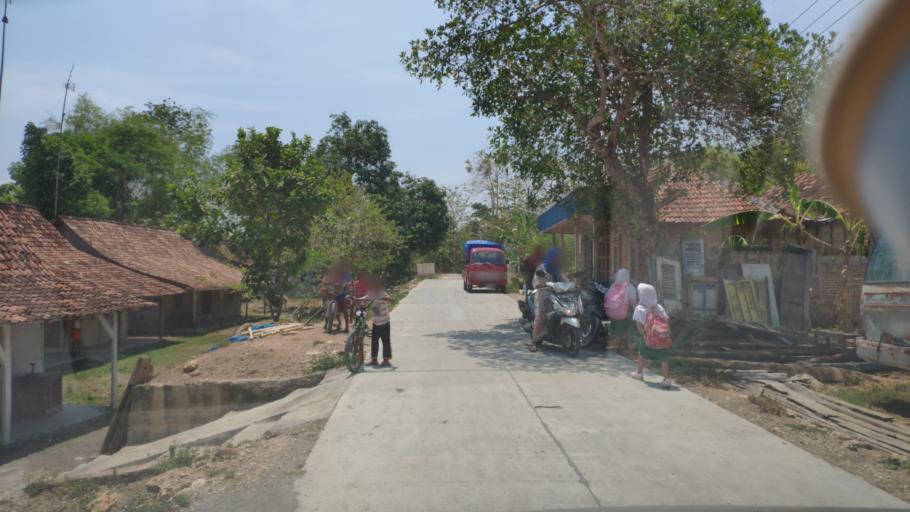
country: ID
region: Central Java
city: Karangtengah
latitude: -7.0414
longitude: 111.3160
